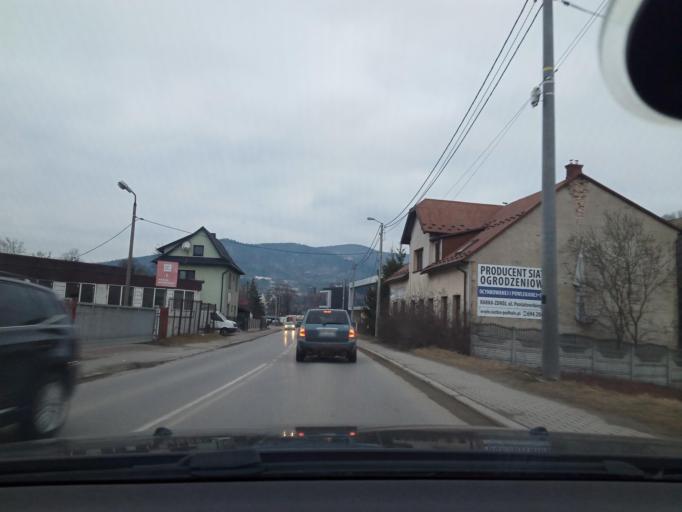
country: PL
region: Lesser Poland Voivodeship
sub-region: Powiat limanowski
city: Mszana Dolna
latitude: 49.6697
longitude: 20.0842
